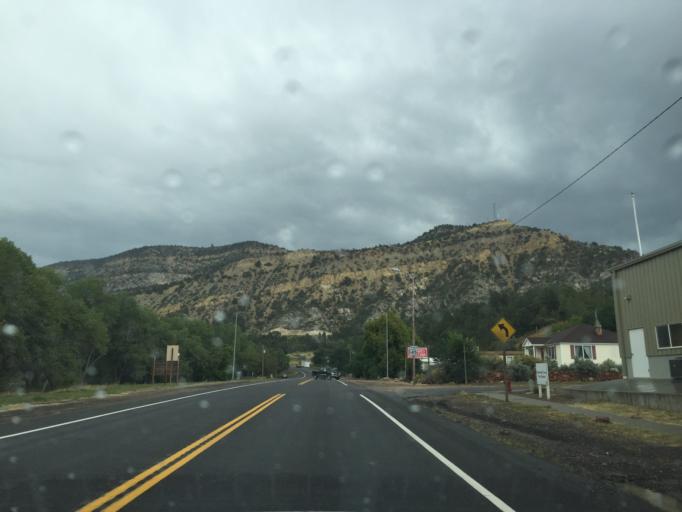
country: US
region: Utah
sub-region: Kane County
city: Kanab
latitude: 37.2759
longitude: -112.6355
